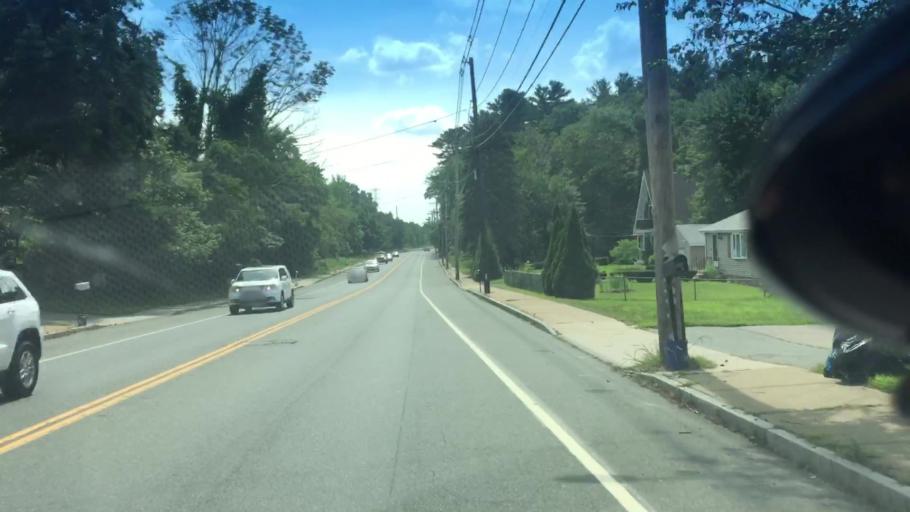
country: US
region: Massachusetts
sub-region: Norfolk County
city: Stoughton
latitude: 42.1486
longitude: -71.0749
